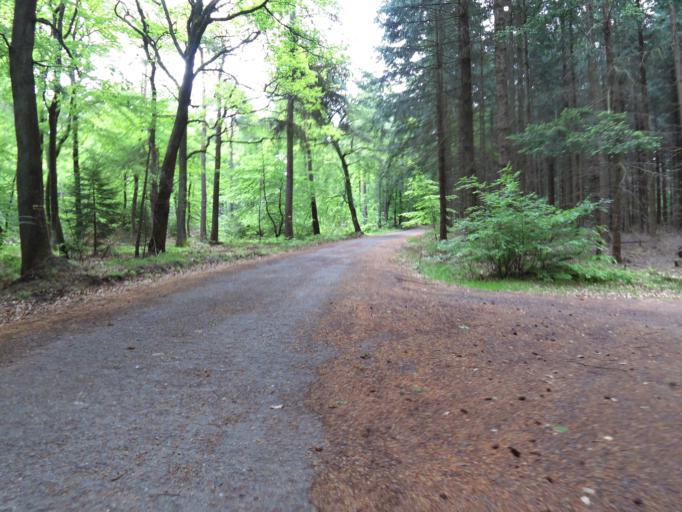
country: DE
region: Rheinland-Pfalz
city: Frankenstein
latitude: 49.4844
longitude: 7.9727
